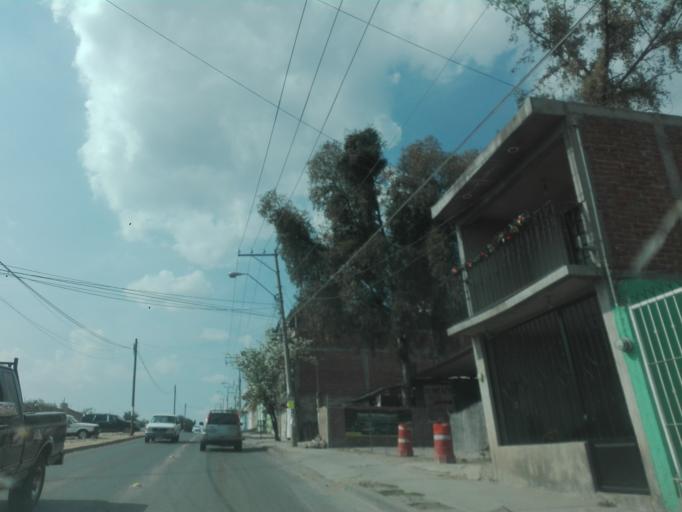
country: MX
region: Guanajuato
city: Leon
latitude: 21.1747
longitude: -101.6747
